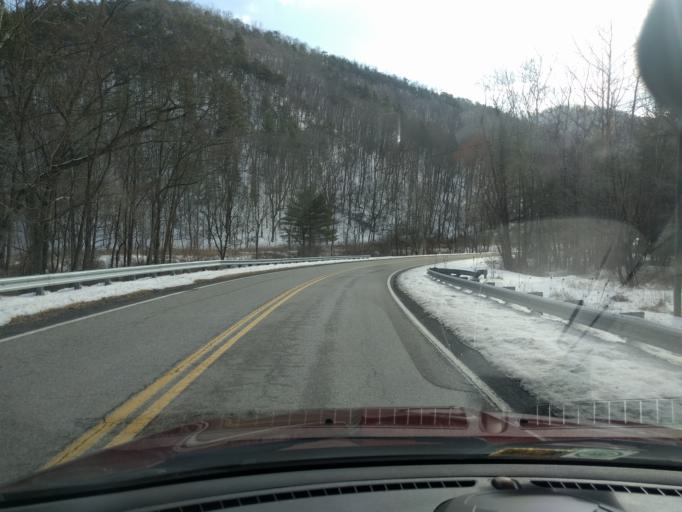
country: US
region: Virginia
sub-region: Bath County
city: Warm Springs
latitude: 38.1222
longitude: -79.9162
